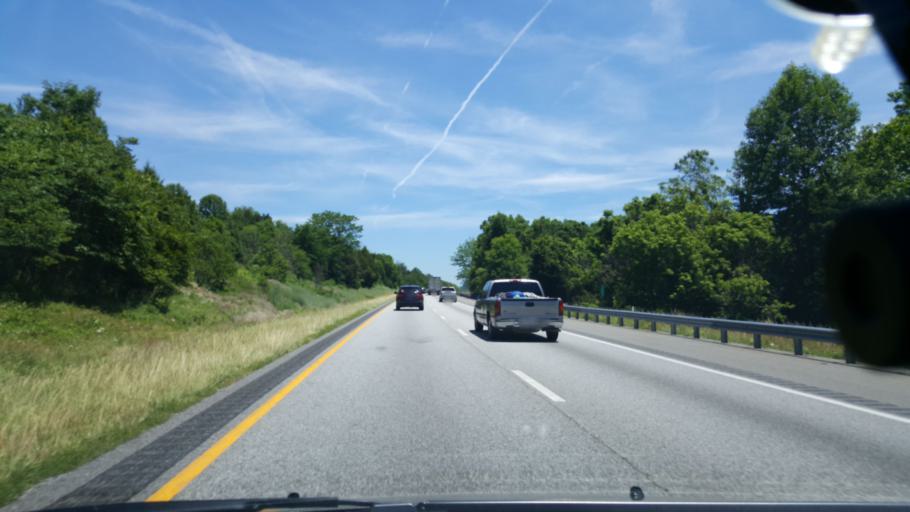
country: US
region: Virginia
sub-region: Botetourt County
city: Fincastle
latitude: 37.4694
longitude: -79.8100
